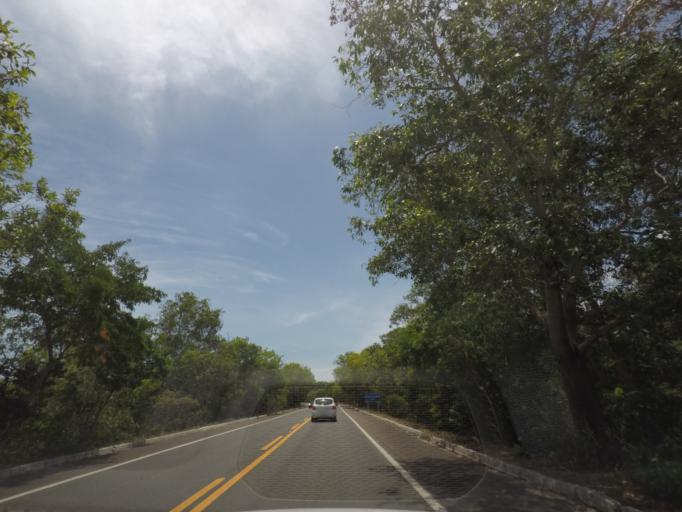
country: BR
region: Bahia
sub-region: Mata De Sao Joao
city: Mata de Sao Joao
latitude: -12.4019
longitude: -37.9236
